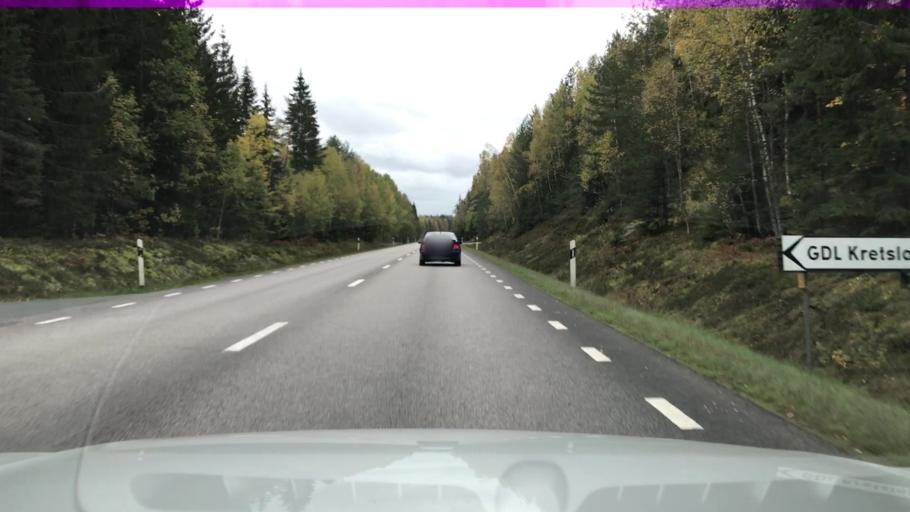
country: SE
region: Kalmar
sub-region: Hultsfreds Kommun
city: Hultsfred
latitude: 57.5472
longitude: 15.8456
